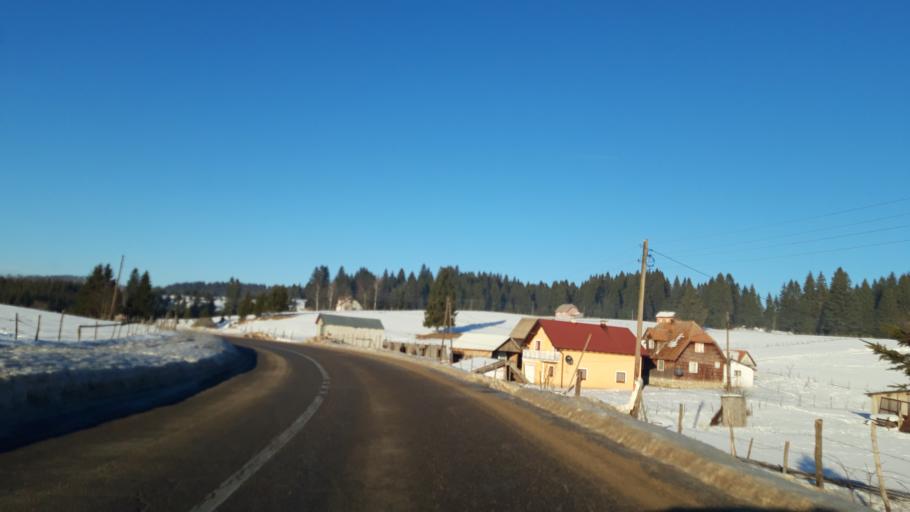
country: BA
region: Republika Srpska
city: Han Pijesak
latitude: 44.1064
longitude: 18.9707
